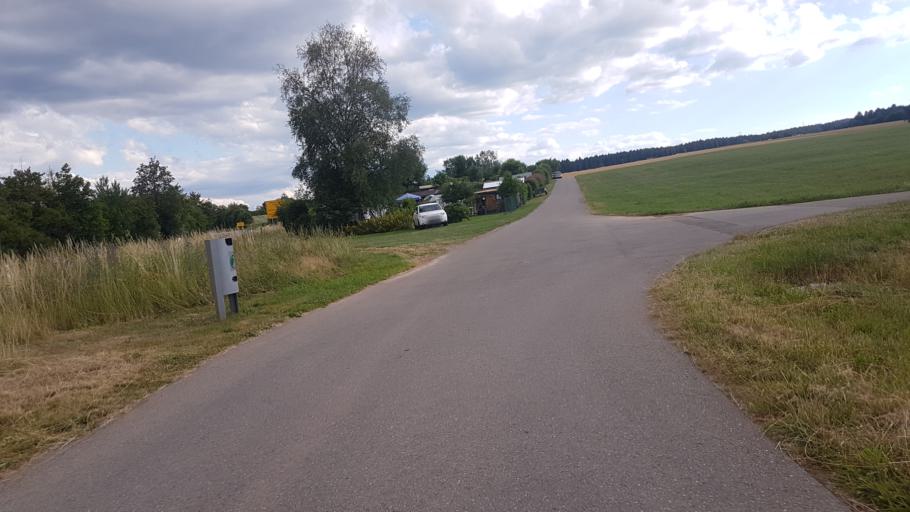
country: DE
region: Baden-Wuerttemberg
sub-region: Freiburg Region
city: Unterkirnach
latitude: 48.0347
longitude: 8.4103
